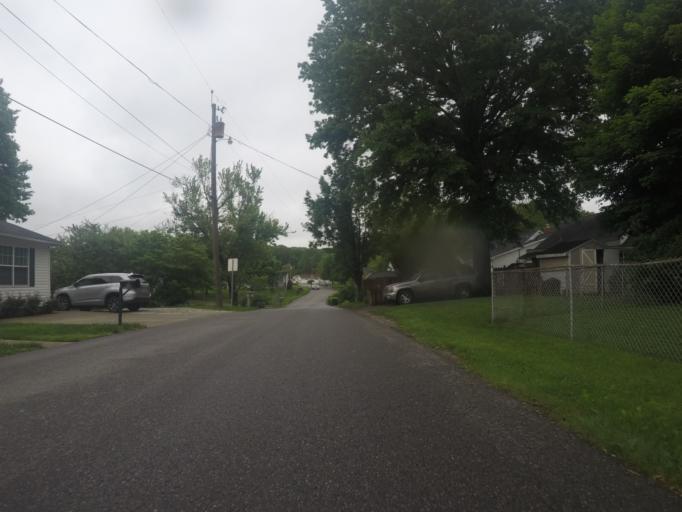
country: US
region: West Virginia
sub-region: Cabell County
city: Barboursville
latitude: 38.4188
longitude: -82.3035
